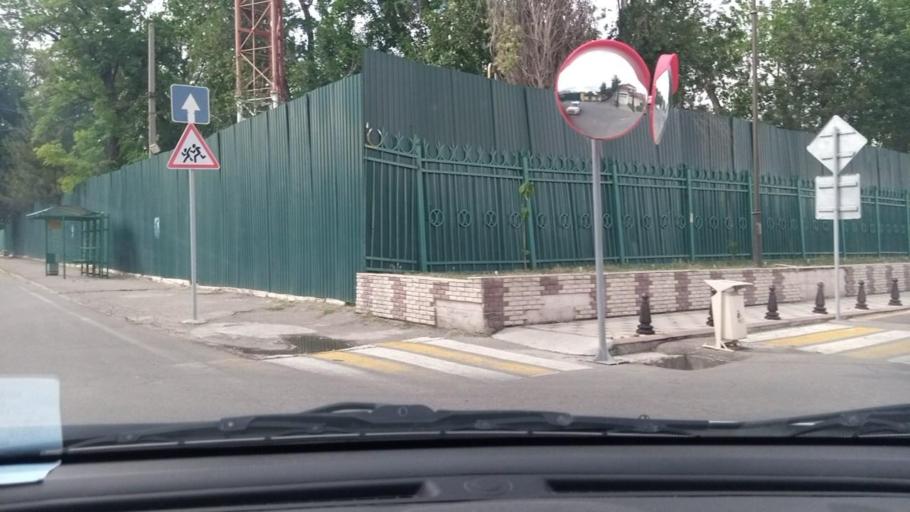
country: UZ
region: Toshkent
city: Salor
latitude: 41.3336
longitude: 69.3588
